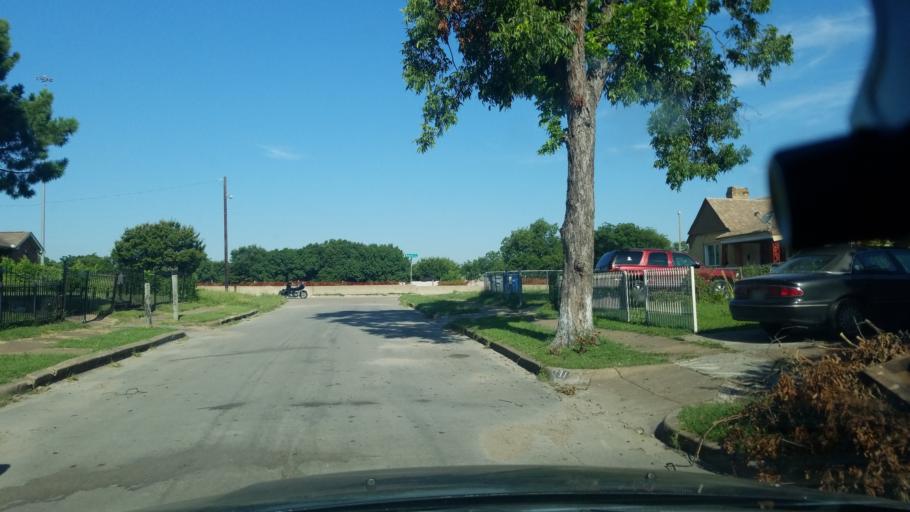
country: US
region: Texas
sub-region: Dallas County
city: Cockrell Hill
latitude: 32.7224
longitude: -96.8258
